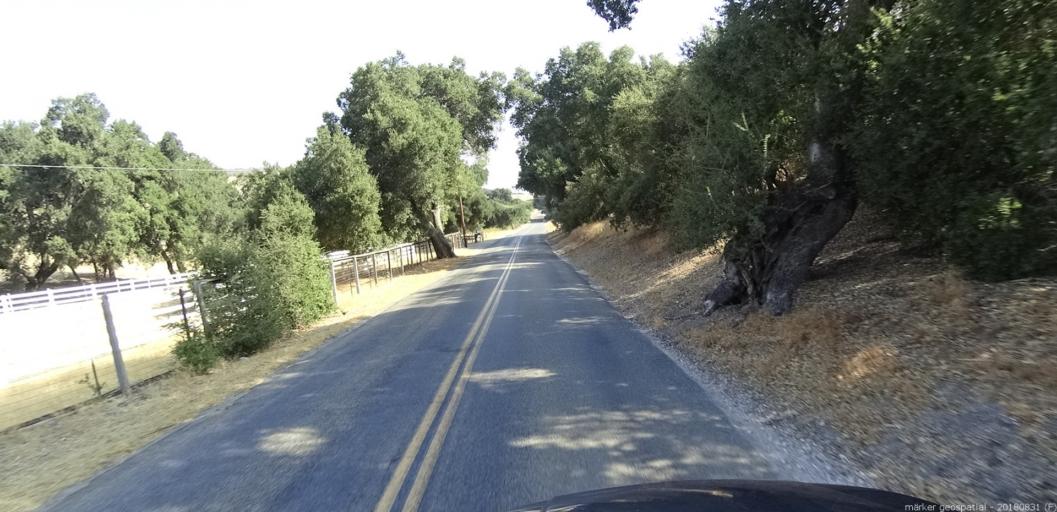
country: US
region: California
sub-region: Monterey County
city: King City
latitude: 36.1625
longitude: -121.1627
